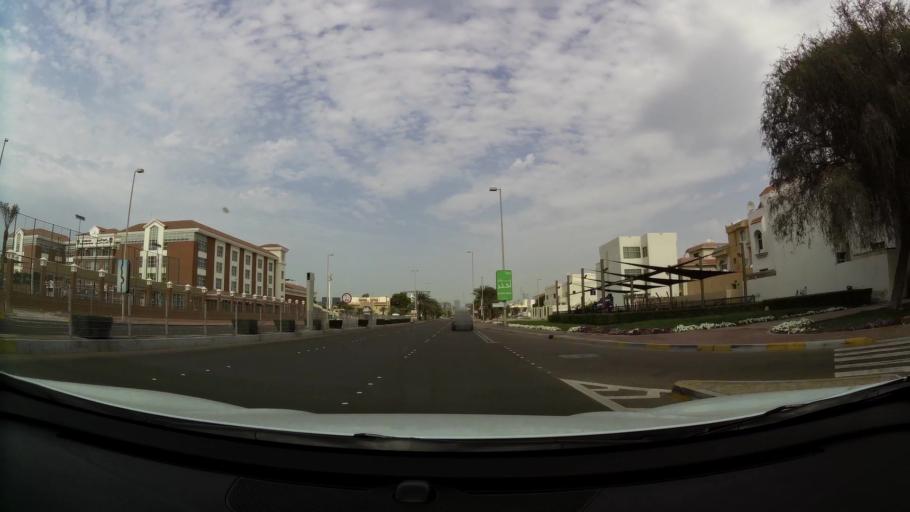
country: AE
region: Abu Dhabi
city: Abu Dhabi
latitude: 24.4630
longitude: 54.3496
